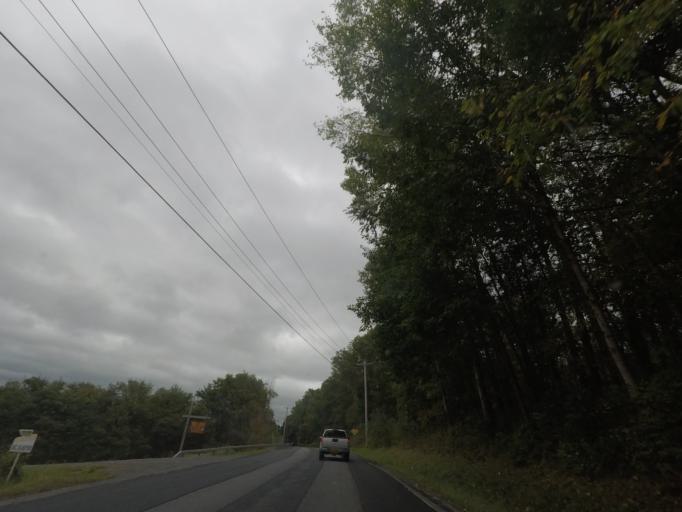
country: US
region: New York
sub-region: Rensselaer County
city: Hoosick Falls
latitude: 42.9498
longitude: -73.4025
